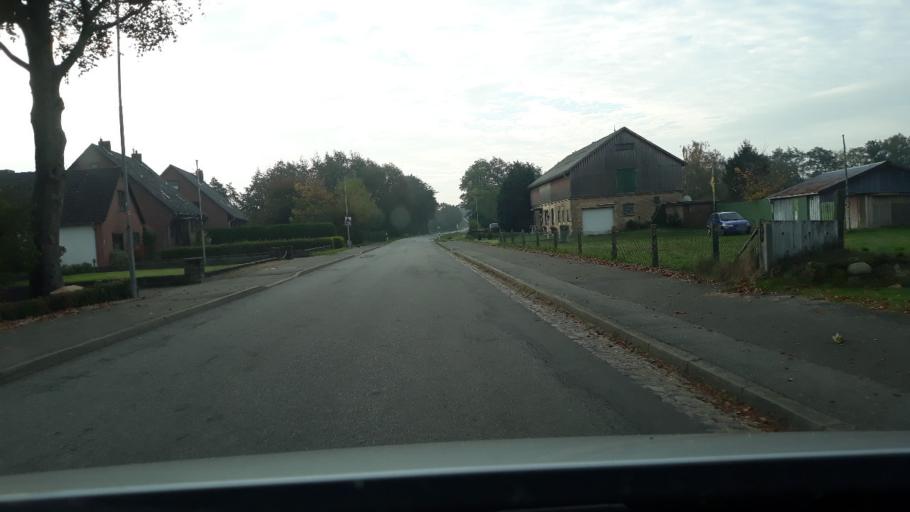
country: DE
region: Schleswig-Holstein
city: Borm
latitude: 54.4035
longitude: 9.3780
